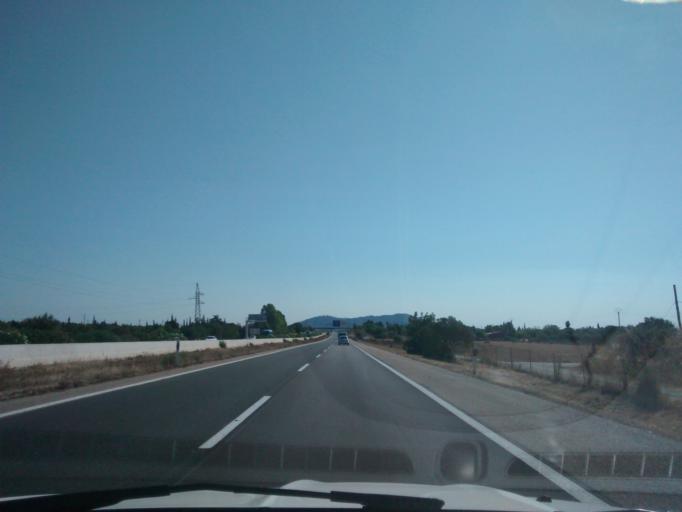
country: ES
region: Balearic Islands
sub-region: Illes Balears
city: Lloseta
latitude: 39.7007
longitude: 2.8900
